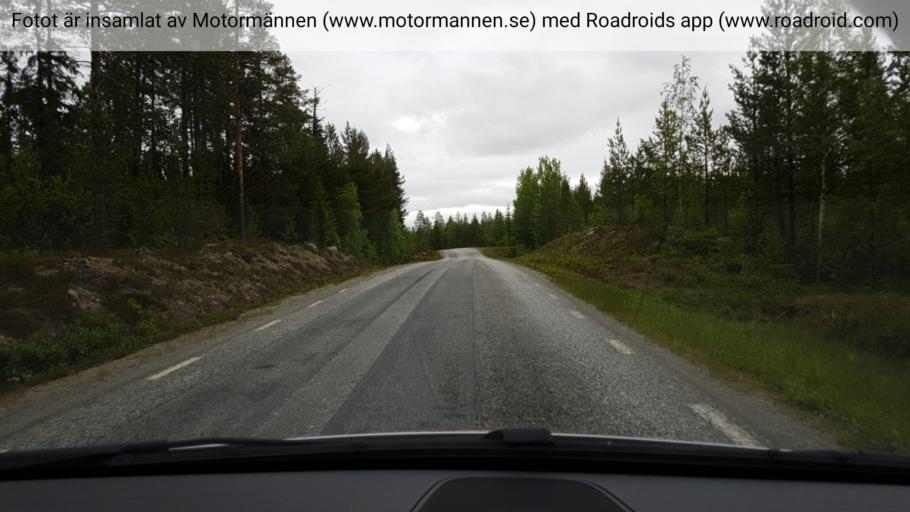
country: SE
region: Jaemtland
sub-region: Harjedalens Kommun
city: Sveg
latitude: 62.3664
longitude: 13.4664
